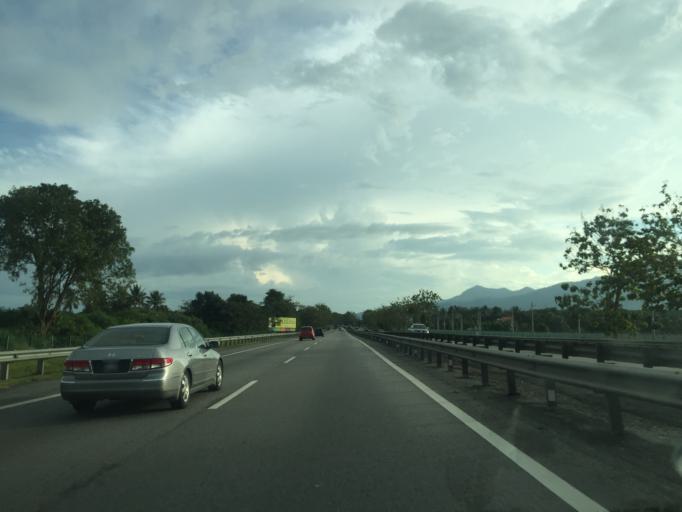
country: MY
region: Kedah
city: Gurun
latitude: 5.8699
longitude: 100.4774
